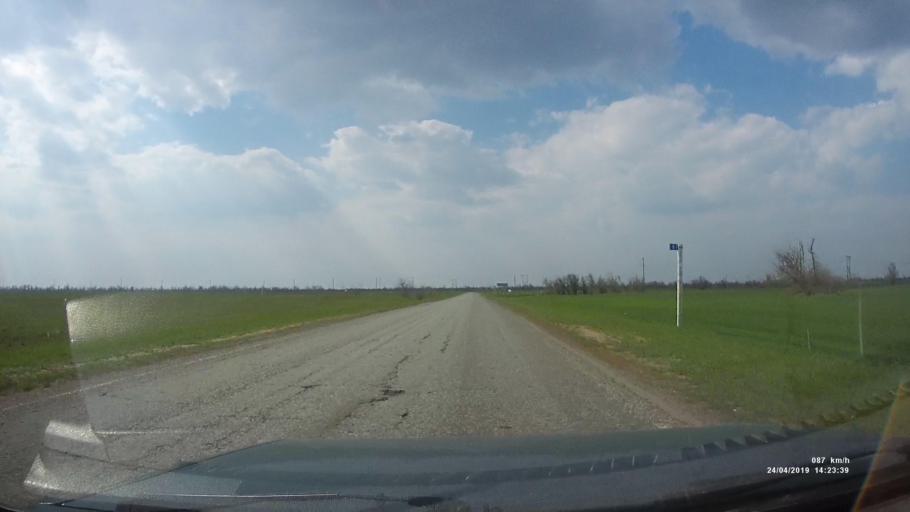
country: RU
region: Kalmykiya
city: Arshan'
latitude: 46.3240
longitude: 44.1112
